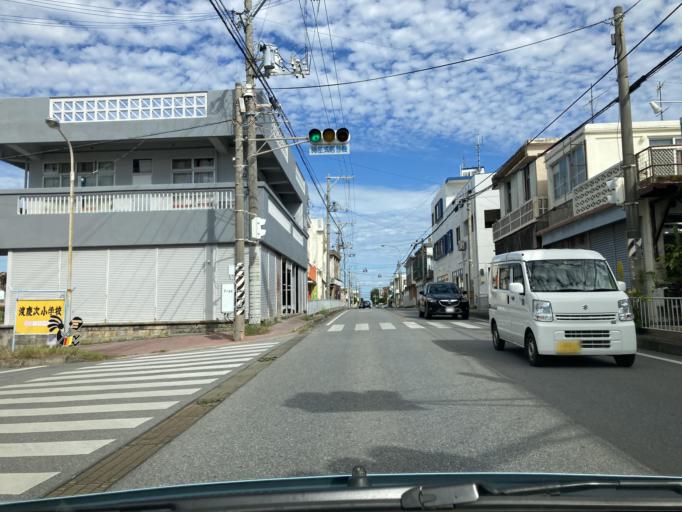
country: JP
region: Okinawa
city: Ishikawa
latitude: 26.4114
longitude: 127.7323
